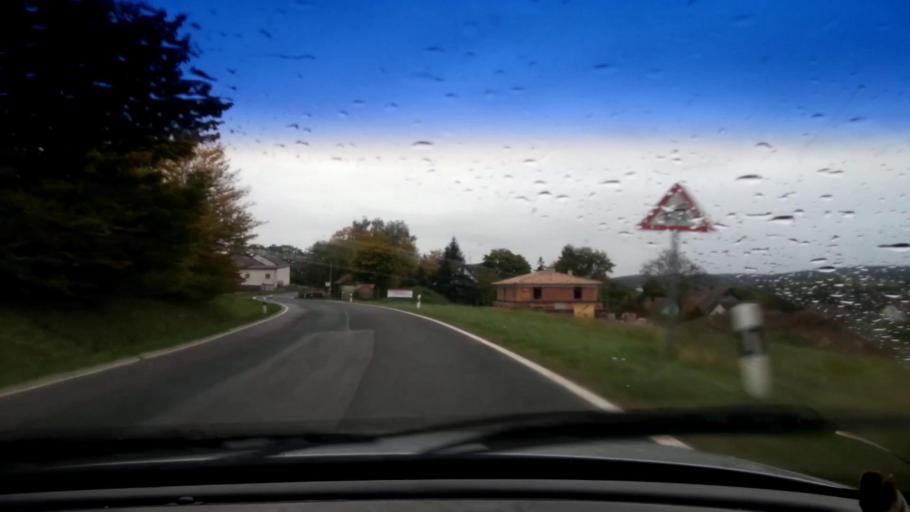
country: DE
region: Bavaria
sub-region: Upper Franconia
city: Priesendorf
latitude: 49.8593
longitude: 10.6846
